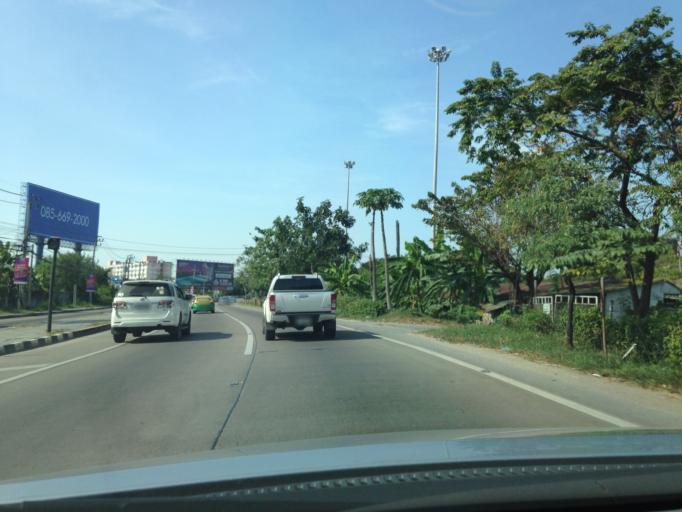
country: TH
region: Nonthaburi
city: Bang Bua Thong
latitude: 13.8709
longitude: 100.4096
